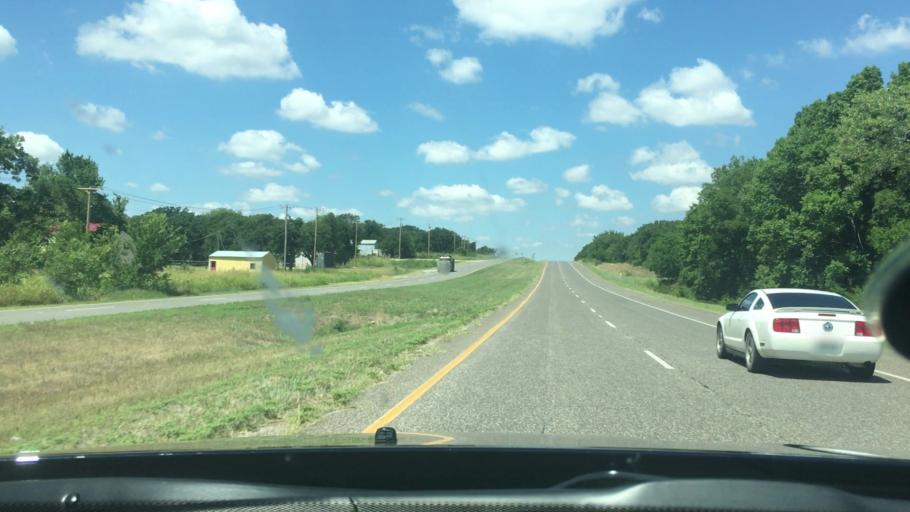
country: US
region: Oklahoma
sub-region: Carter County
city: Lone Grove
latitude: 34.1731
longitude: -97.2878
